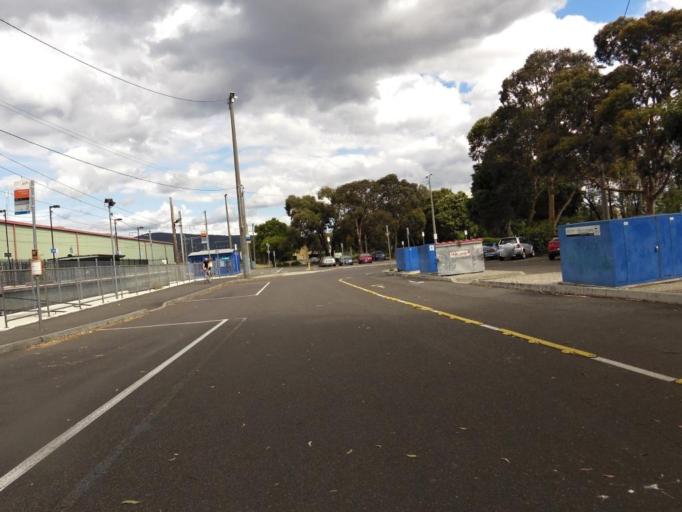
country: AU
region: Victoria
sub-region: Knox
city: Bayswater
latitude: -37.8422
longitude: 145.2682
